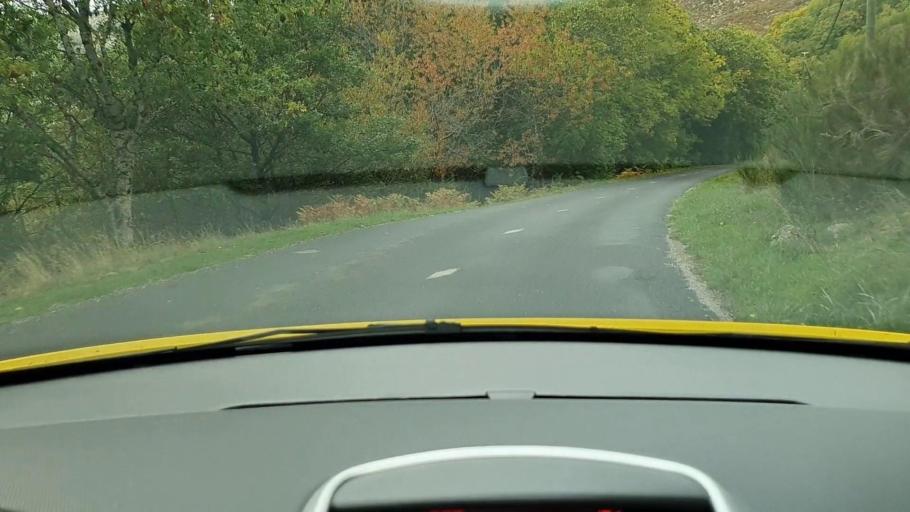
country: FR
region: Languedoc-Roussillon
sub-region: Departement de la Lozere
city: Meyrueis
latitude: 44.0687
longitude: 3.4568
